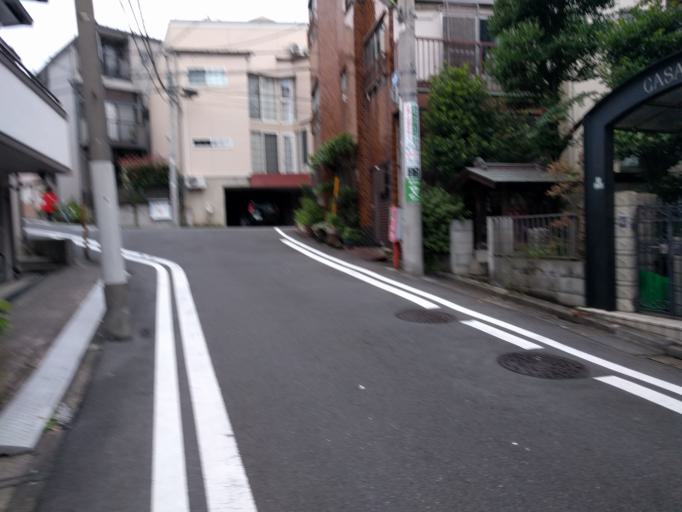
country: JP
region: Tokyo
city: Tokyo
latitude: 35.6392
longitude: 139.6758
